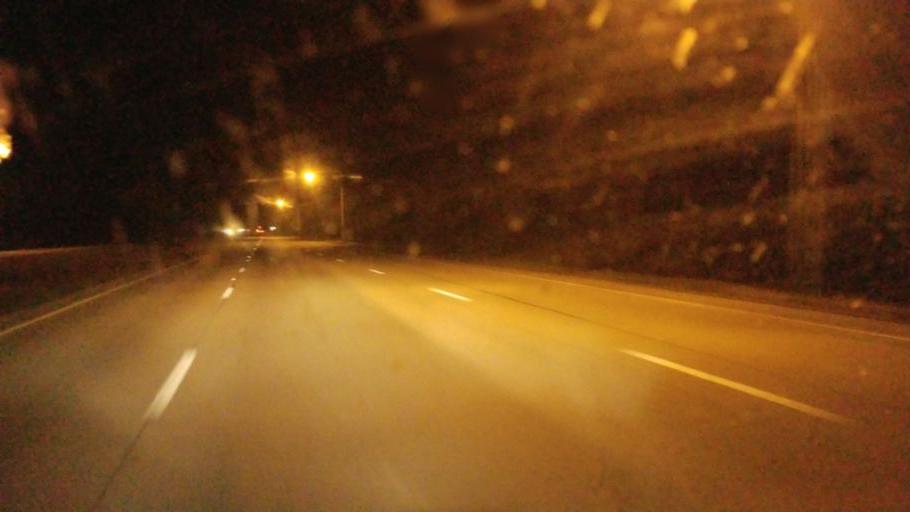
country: US
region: Ohio
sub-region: Allen County
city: Delphos
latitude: 40.8735
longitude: -84.3553
